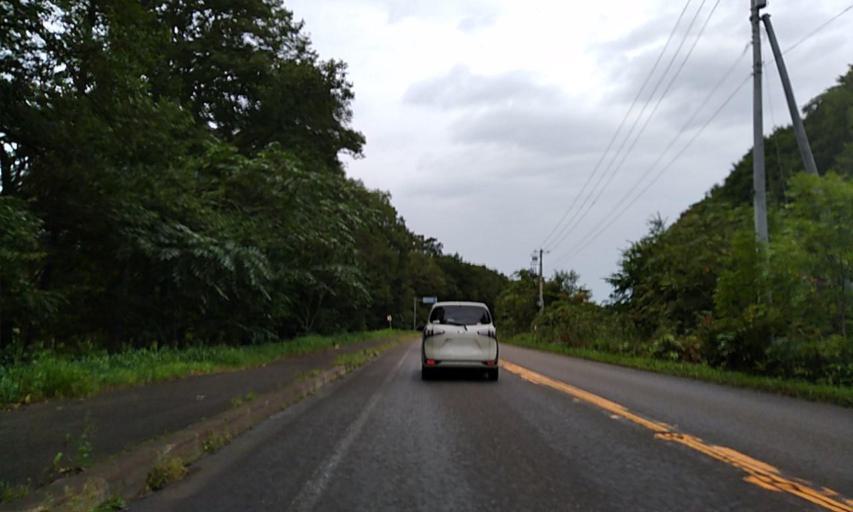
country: JP
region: Hokkaido
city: Abashiri
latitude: 43.9763
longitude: 144.2169
